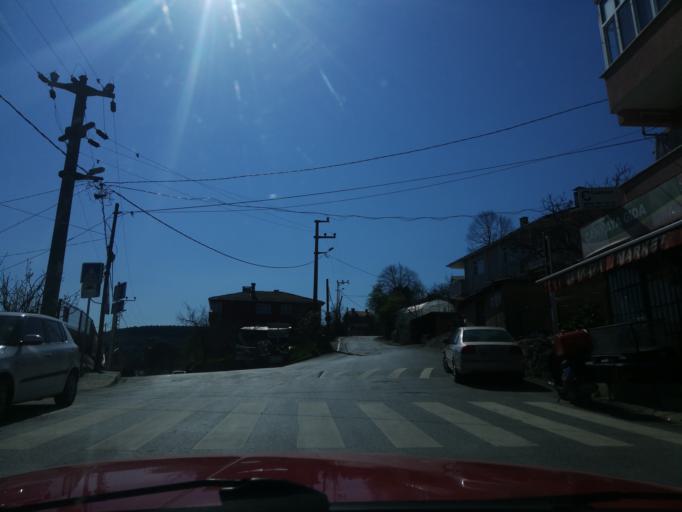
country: TR
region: Istanbul
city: Mahmut Sevket Pasa
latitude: 41.1273
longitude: 29.1591
